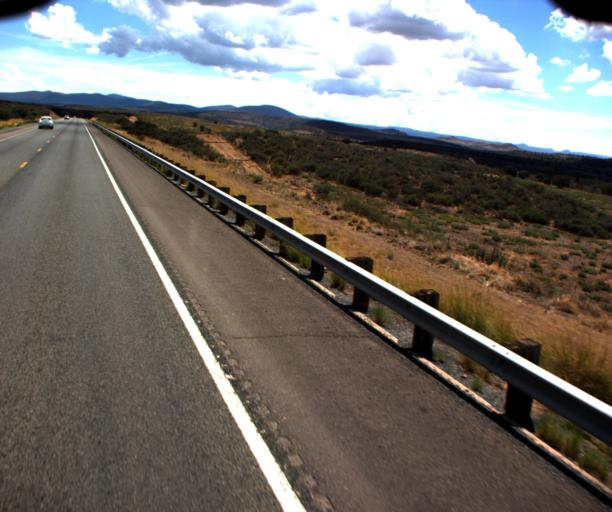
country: US
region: Arizona
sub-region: Yavapai County
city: Dewey-Humboldt
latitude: 34.5237
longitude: -112.0772
